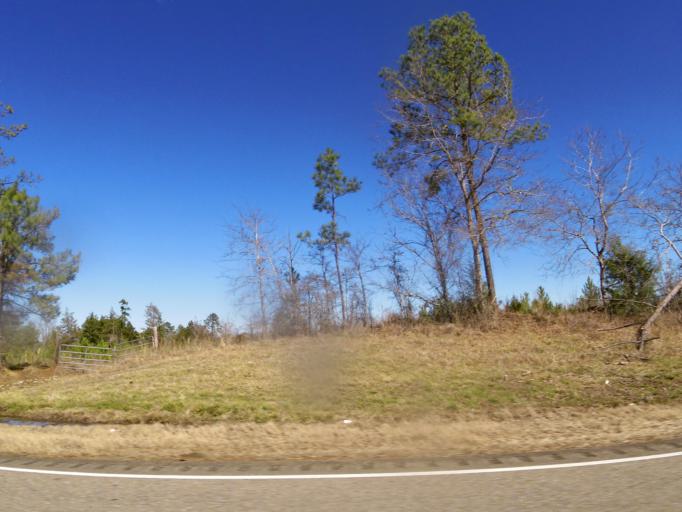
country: US
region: Alabama
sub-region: Montgomery County
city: Pike Road
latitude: 32.1728
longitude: -86.0760
